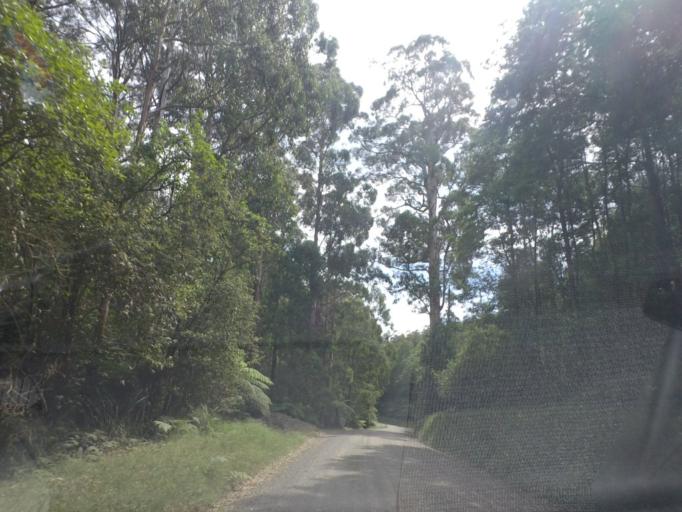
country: AU
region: Victoria
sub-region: Yarra Ranges
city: Healesville
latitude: -37.5366
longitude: 145.5135
